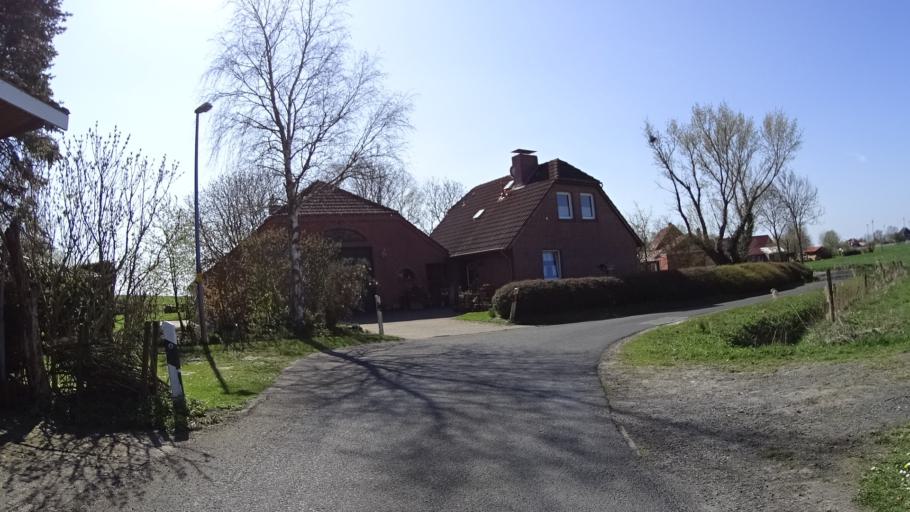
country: DE
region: Lower Saxony
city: Leer
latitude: 53.2034
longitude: 7.4042
